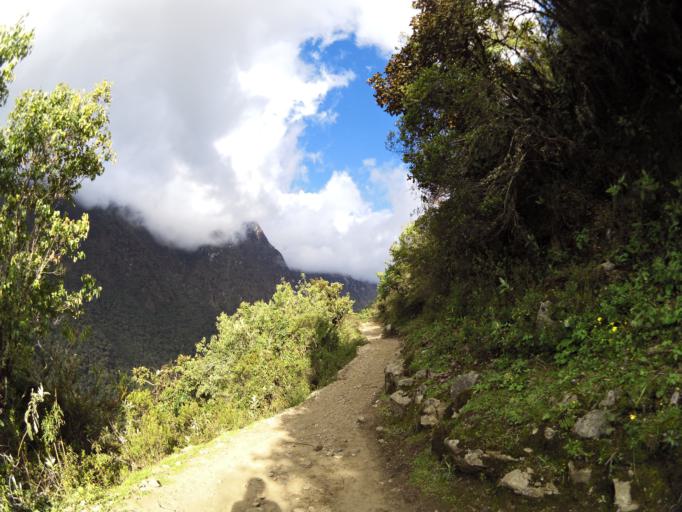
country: PE
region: Cusco
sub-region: Provincia de La Convencion
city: Santa Teresa
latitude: -13.3144
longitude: -72.6267
